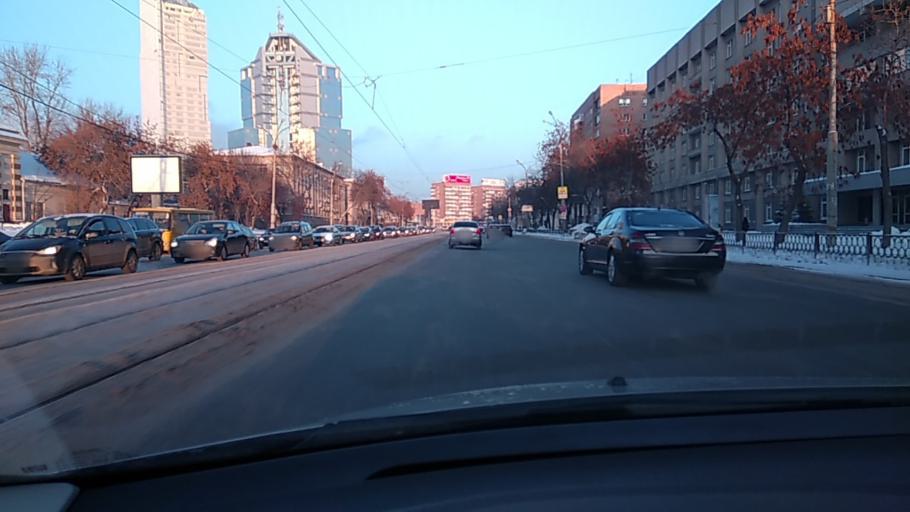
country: RU
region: Sverdlovsk
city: Yekaterinburg
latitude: 56.8530
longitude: 60.5967
